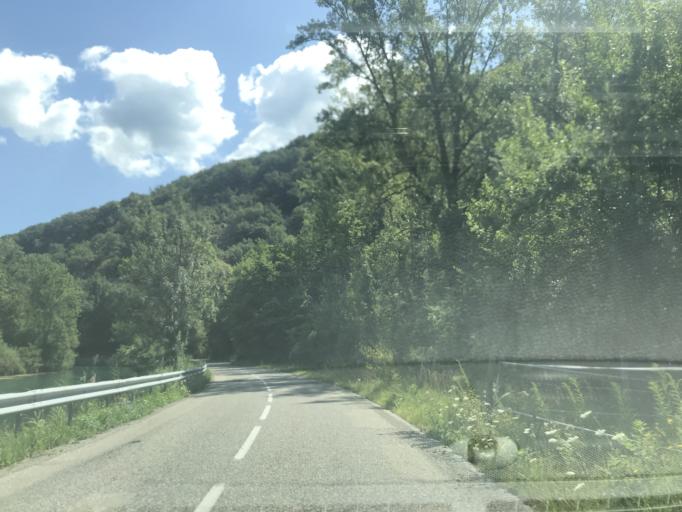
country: FR
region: Rhone-Alpes
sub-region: Departement de l'Ain
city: Culoz
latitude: 45.8140
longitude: 5.8032
